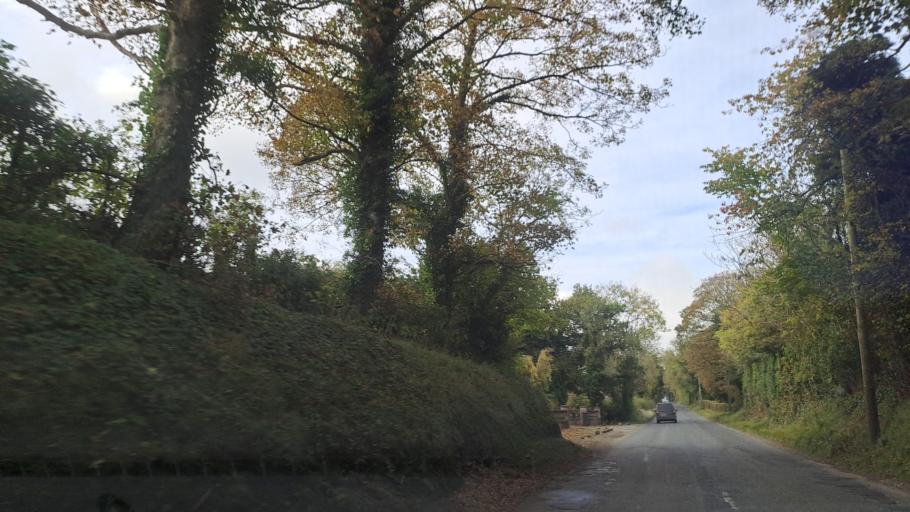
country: IE
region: Ulster
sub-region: An Cabhan
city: Kingscourt
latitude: 53.8374
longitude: -6.7672
